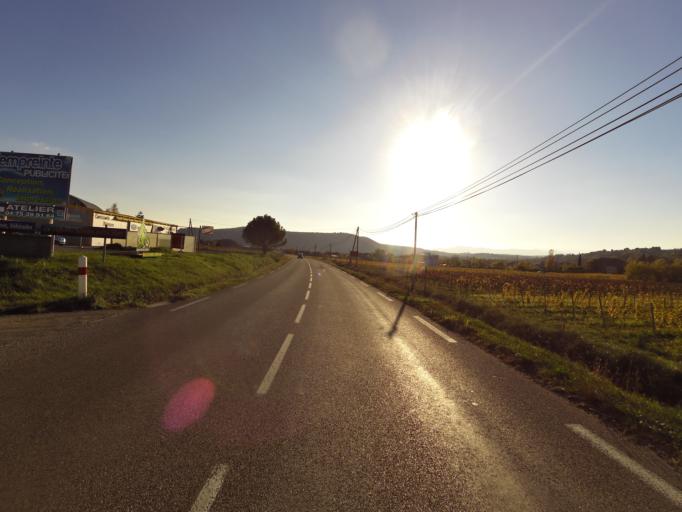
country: FR
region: Rhone-Alpes
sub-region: Departement de l'Ardeche
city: Rosieres
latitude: 44.4890
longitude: 4.2714
